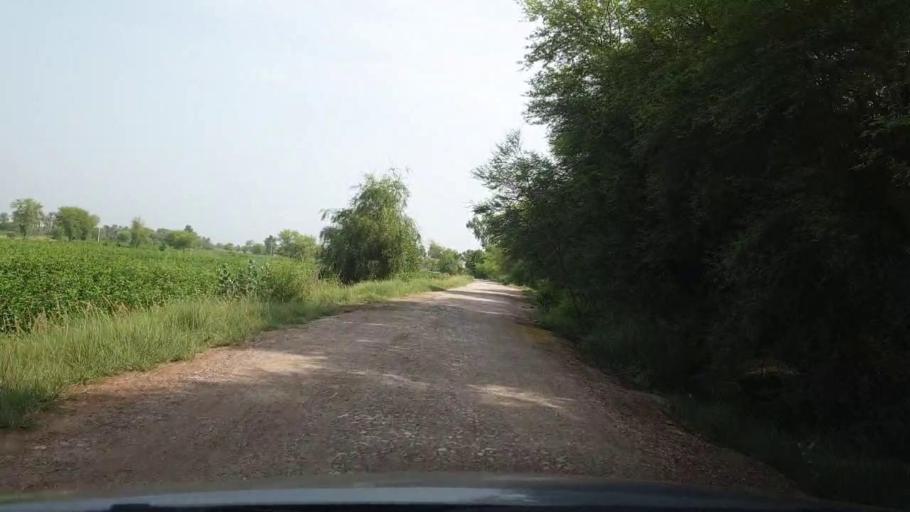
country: PK
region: Sindh
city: Rohri
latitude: 27.6541
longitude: 69.0240
